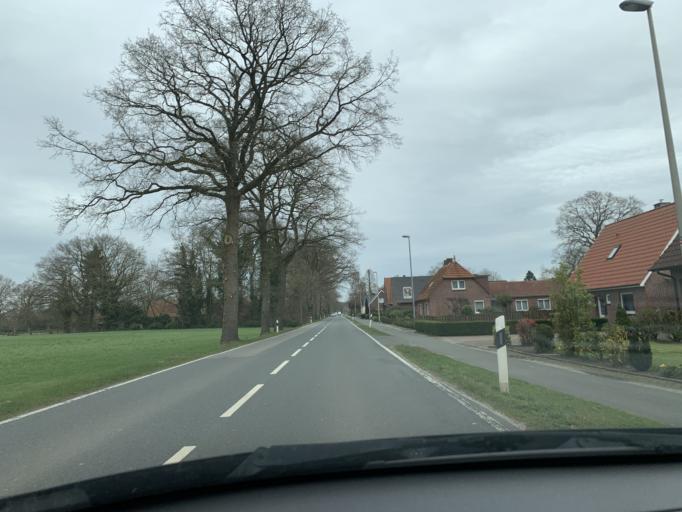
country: DE
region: Lower Saxony
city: Bad Zwischenahn
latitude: 53.1743
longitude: 7.9676
